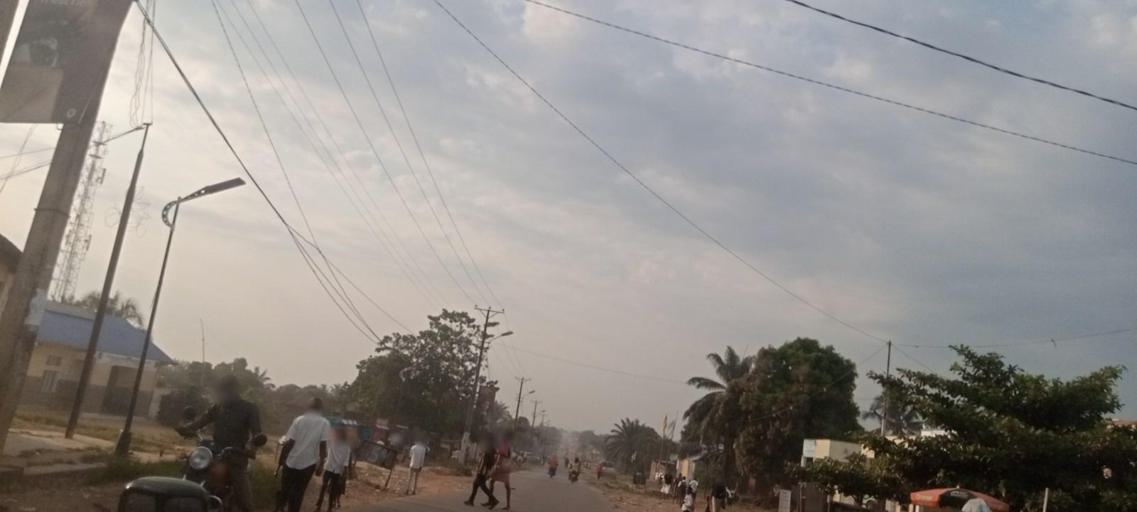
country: CD
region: Kasai-Oriental
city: Mbuji-Mayi
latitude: -6.1259
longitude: 23.5993
